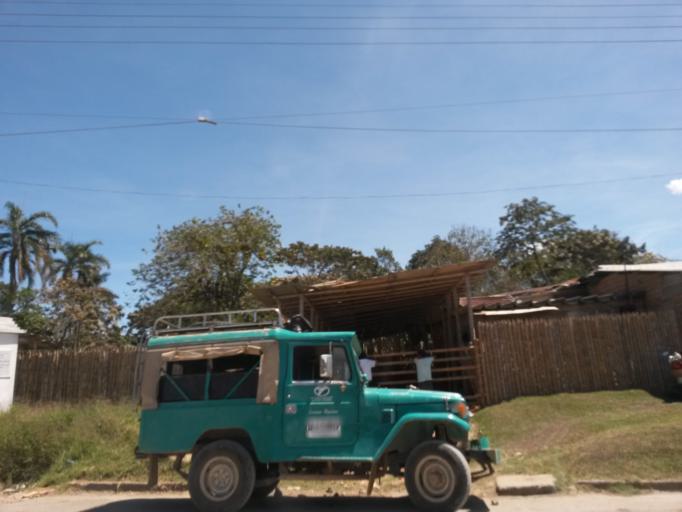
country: CO
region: Cauca
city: El Tambo
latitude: 2.4488
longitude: -76.8162
